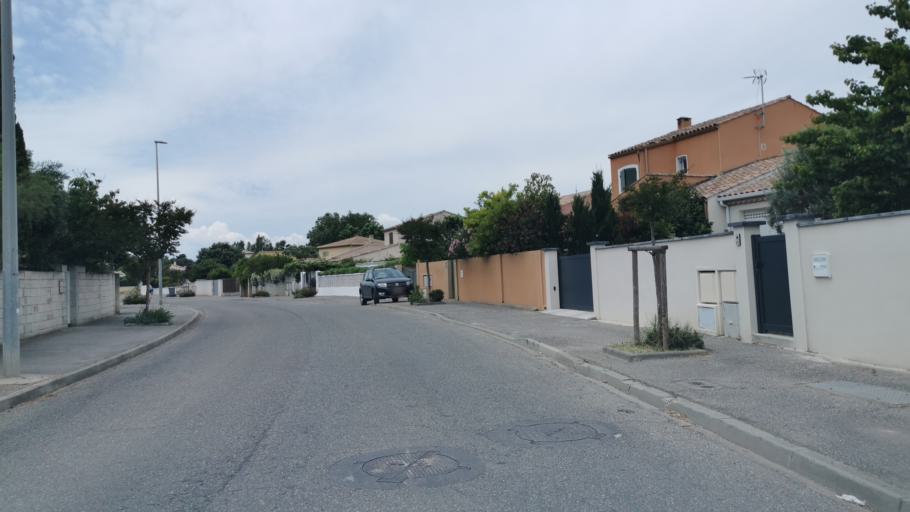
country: FR
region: Languedoc-Roussillon
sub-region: Departement de l'Aude
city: Narbonne
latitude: 43.1968
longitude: 3.0212
